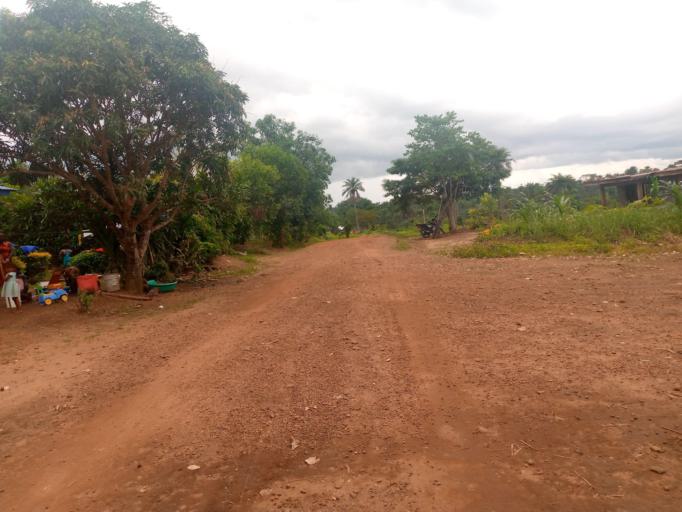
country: SL
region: Southern Province
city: Mogbwemo
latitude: 7.6179
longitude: -12.1778
